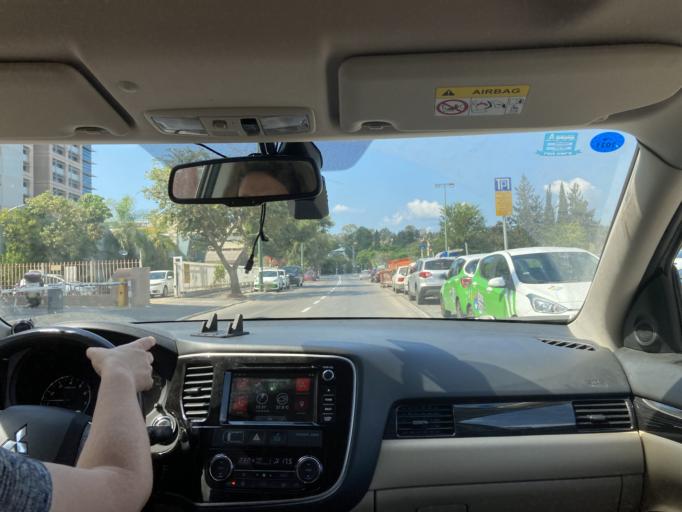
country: IL
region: Tel Aviv
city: Bene Beraq
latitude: 32.1114
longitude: 34.8410
